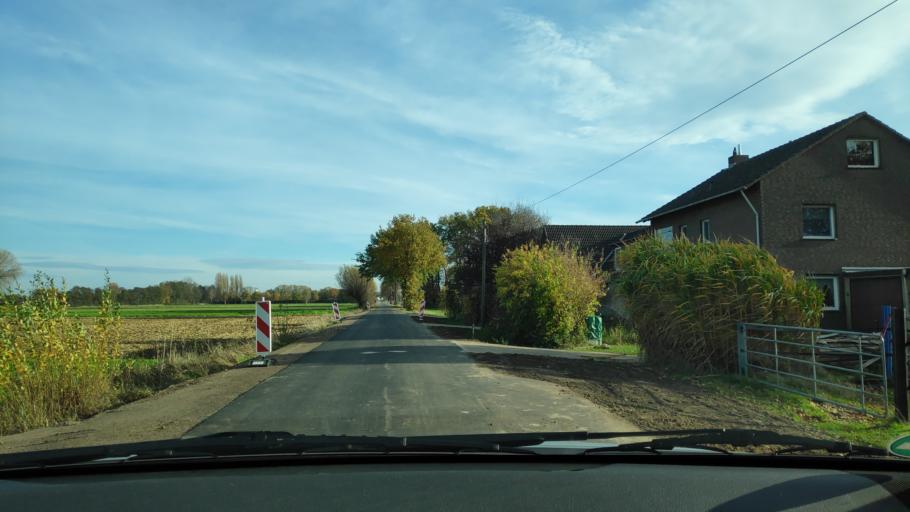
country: DE
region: North Rhine-Westphalia
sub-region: Regierungsbezirk Detmold
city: Minden
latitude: 52.2840
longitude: 8.8543
